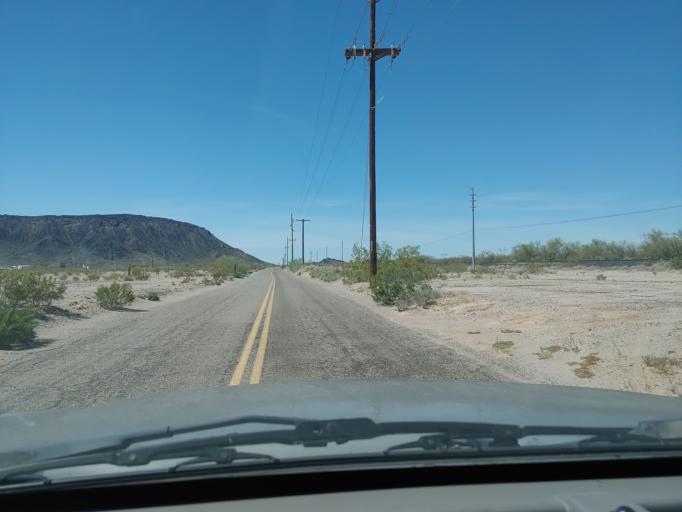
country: US
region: Arizona
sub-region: Maricopa County
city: Gila Bend
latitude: 33.0235
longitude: -113.3339
